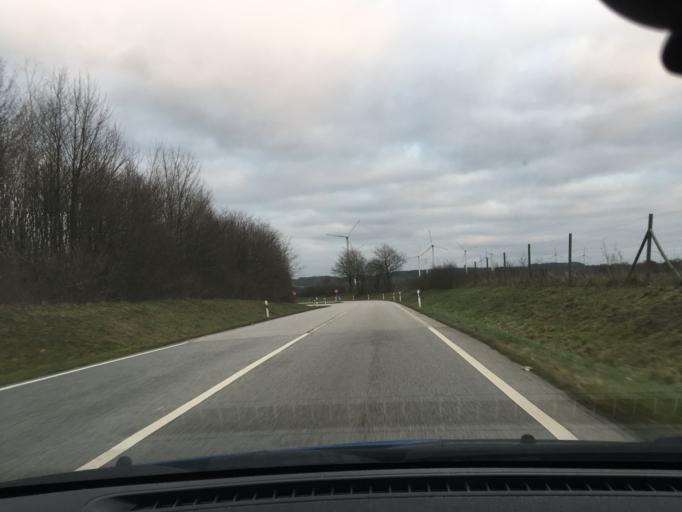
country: DE
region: Schleswig-Holstein
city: Besdorf
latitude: 54.0575
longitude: 9.3632
